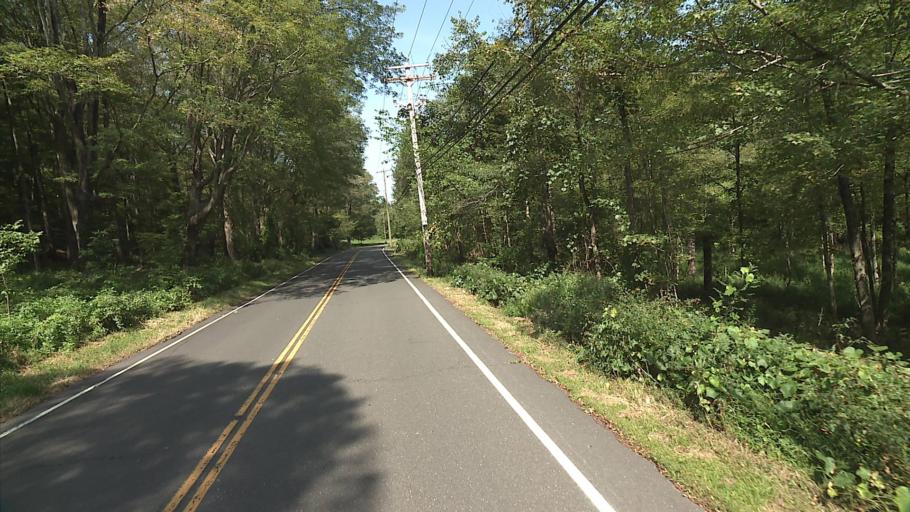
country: US
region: Connecticut
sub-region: Fairfield County
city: Georgetown
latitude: 41.2521
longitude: -73.3233
